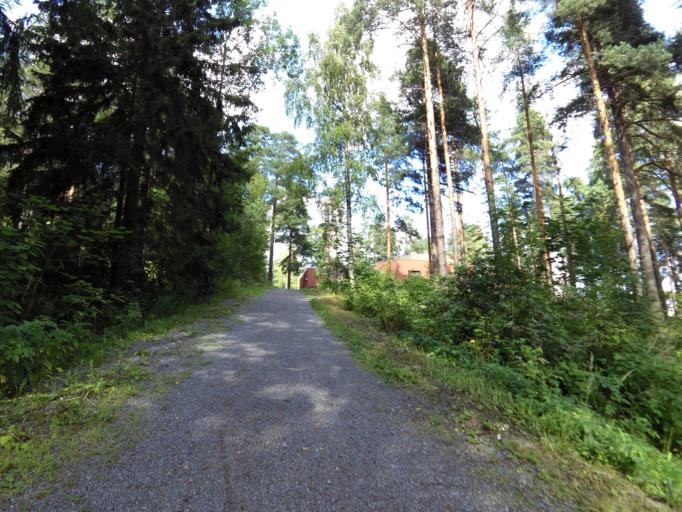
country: FI
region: Pirkanmaa
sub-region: Tampere
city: Pirkkala
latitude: 61.5048
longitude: 23.6242
